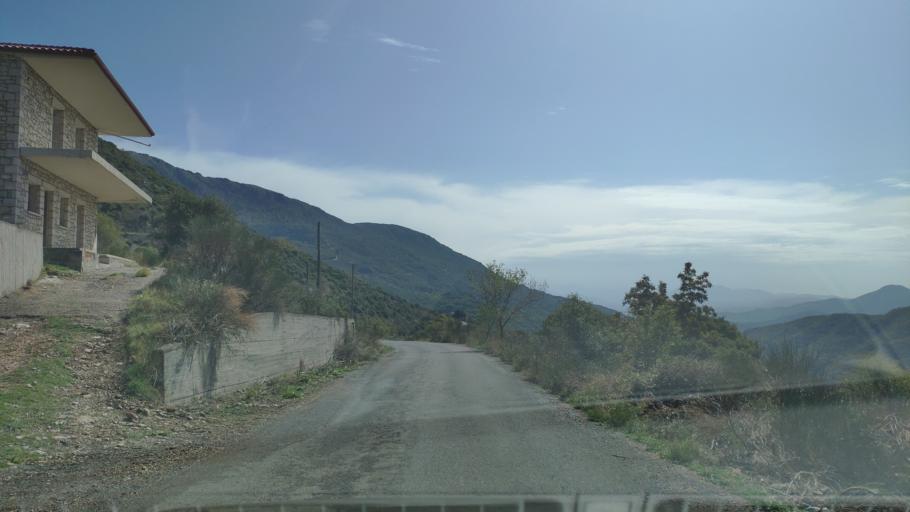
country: GR
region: Peloponnese
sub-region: Nomos Arkadias
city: Dimitsana
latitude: 37.5880
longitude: 22.0445
